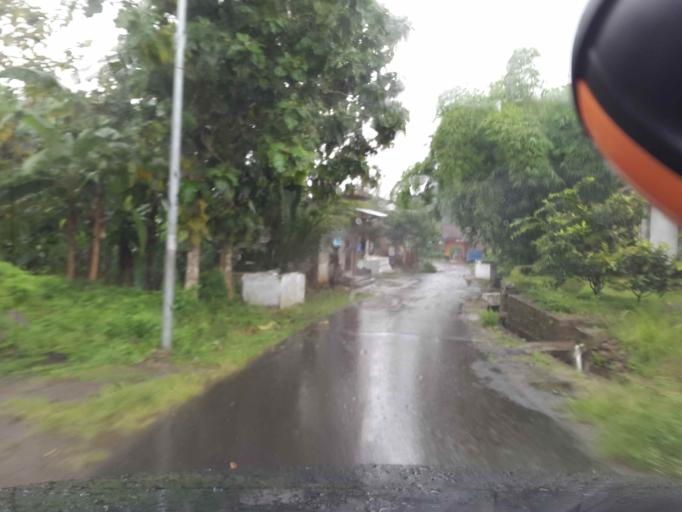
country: ID
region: Central Java
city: Salatiga
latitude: -7.3017
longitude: 110.4757
